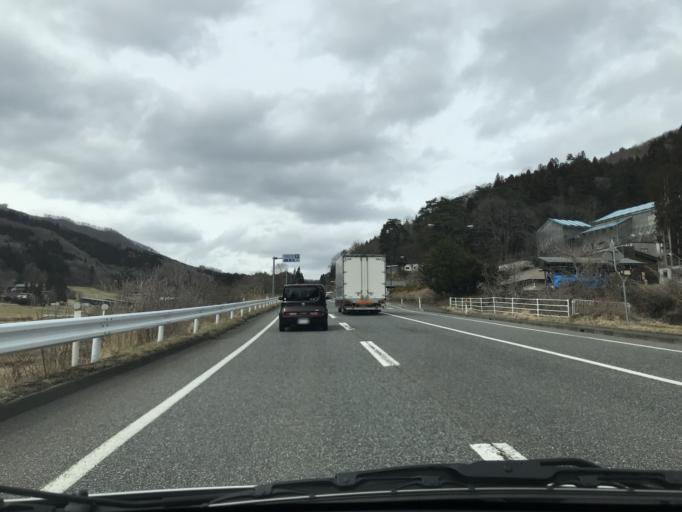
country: JP
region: Iwate
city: Tono
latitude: 39.3390
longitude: 141.4425
